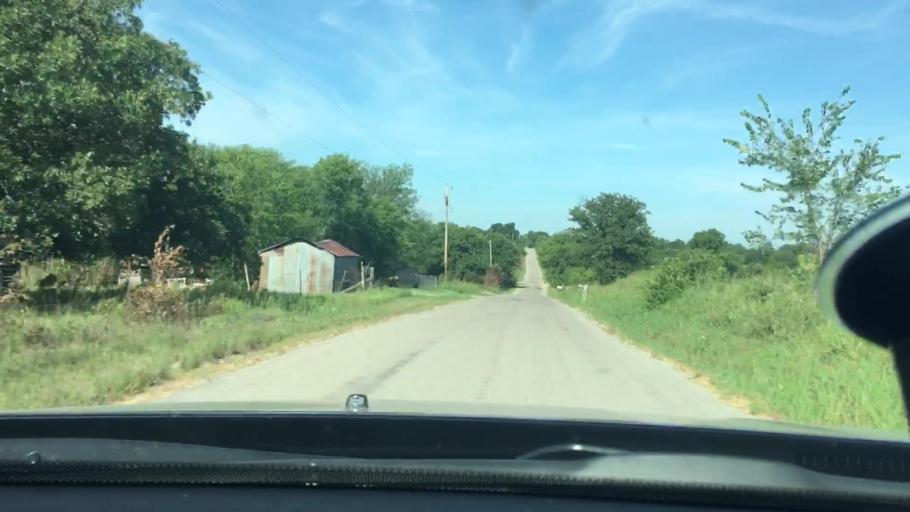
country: US
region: Oklahoma
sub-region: Carter County
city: Lone Grove
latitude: 34.2674
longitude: -97.2566
